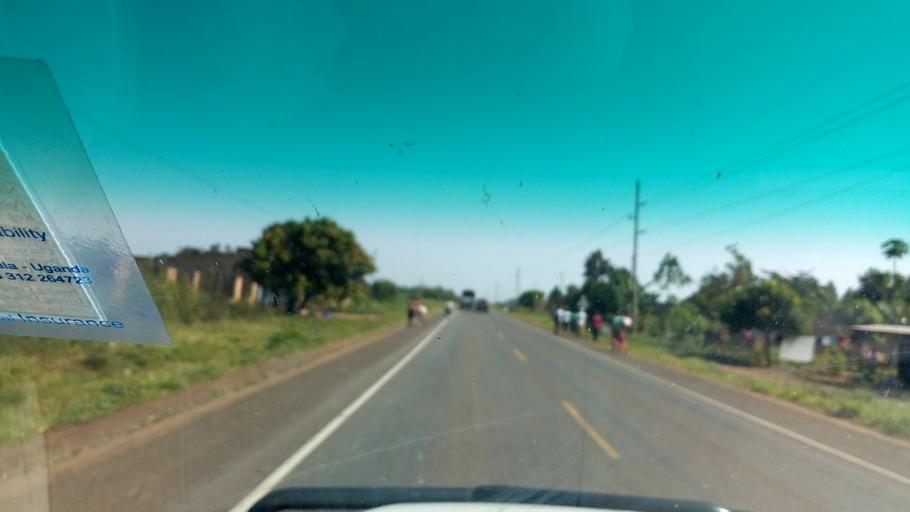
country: UG
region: Western Region
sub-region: Kiryandongo District
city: Kiryandongo
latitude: 1.9336
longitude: 32.1241
